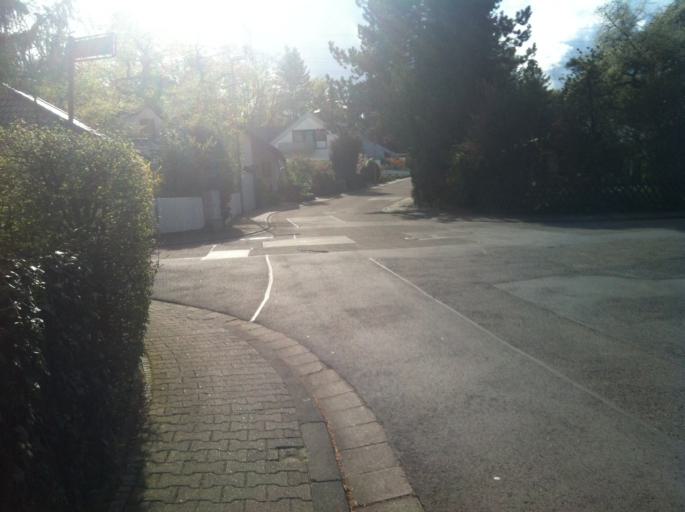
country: DE
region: Rheinland-Pfalz
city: Budenheim
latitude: 49.9995
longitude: 8.1892
